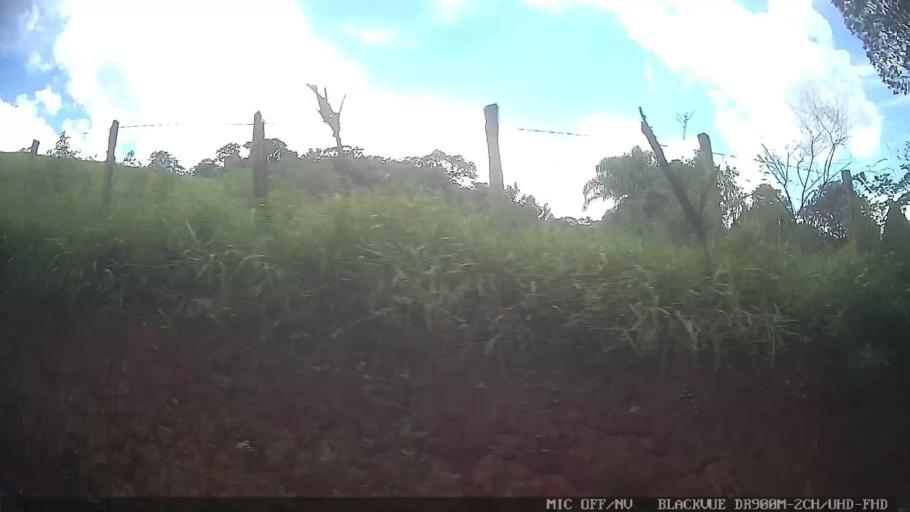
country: BR
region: Minas Gerais
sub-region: Extrema
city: Extrema
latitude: -22.8270
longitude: -46.2369
